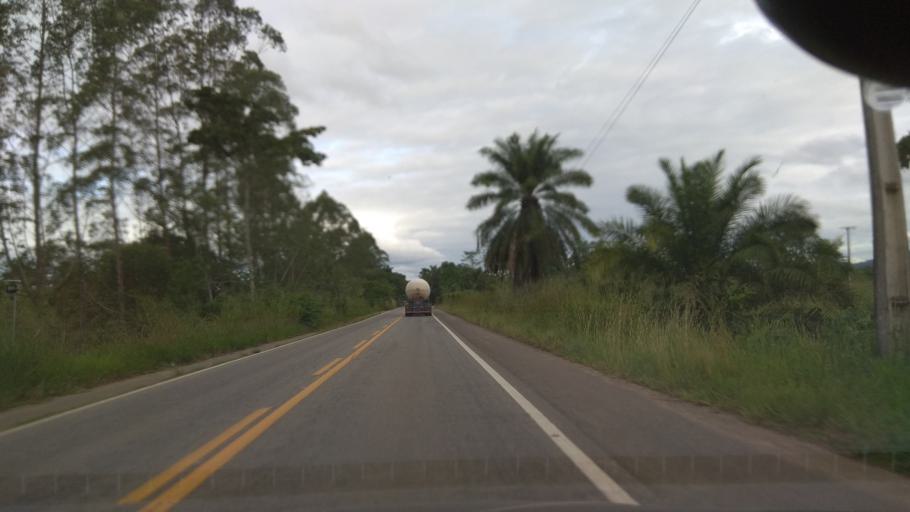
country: BR
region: Bahia
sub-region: Ipiau
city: Ipiau
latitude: -14.1630
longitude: -39.6902
